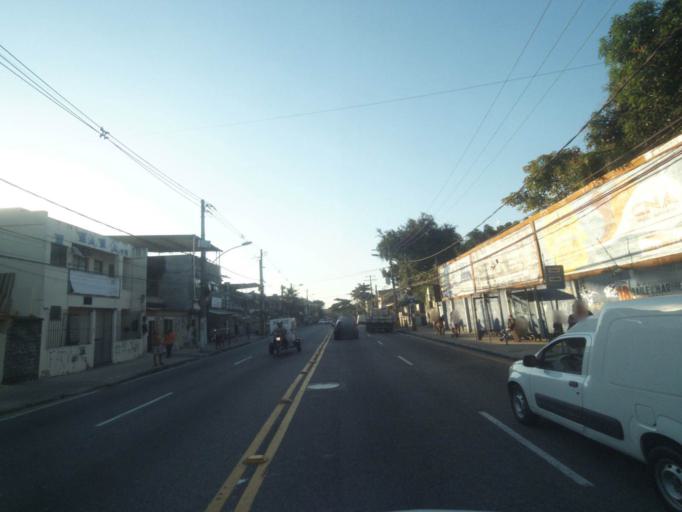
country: BR
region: Rio de Janeiro
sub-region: Sao Joao De Meriti
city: Sao Joao de Meriti
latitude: -22.9502
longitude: -43.3592
